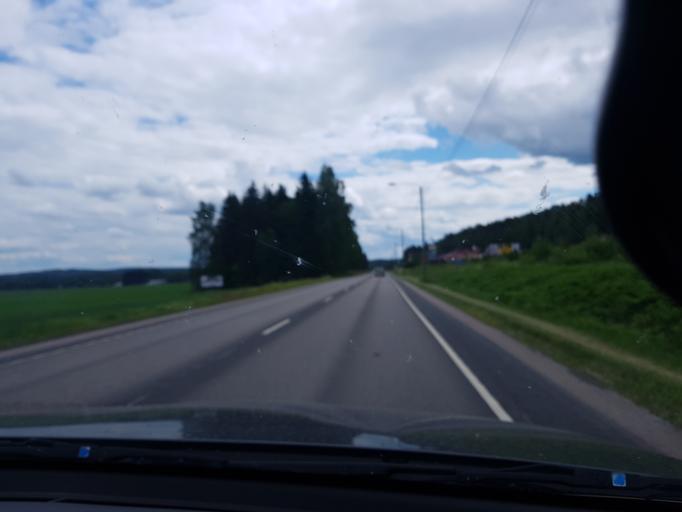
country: FI
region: Pirkanmaa
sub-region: Tampere
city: Paelkaene
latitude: 61.3504
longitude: 24.2537
